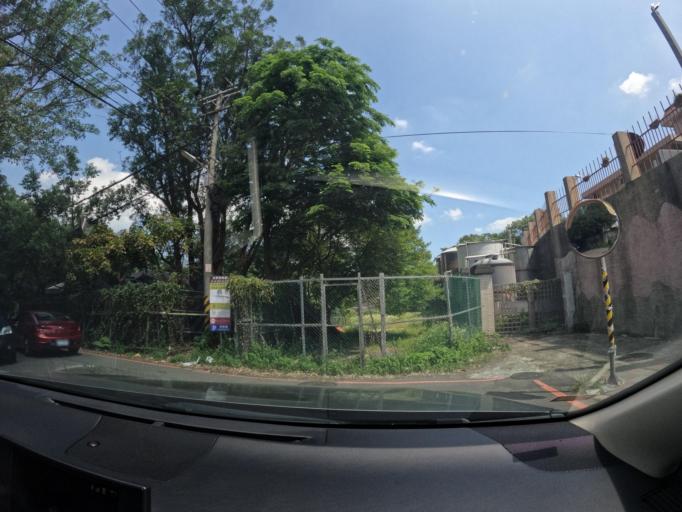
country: TW
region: Taipei
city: Taipei
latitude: 25.1355
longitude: 121.5420
